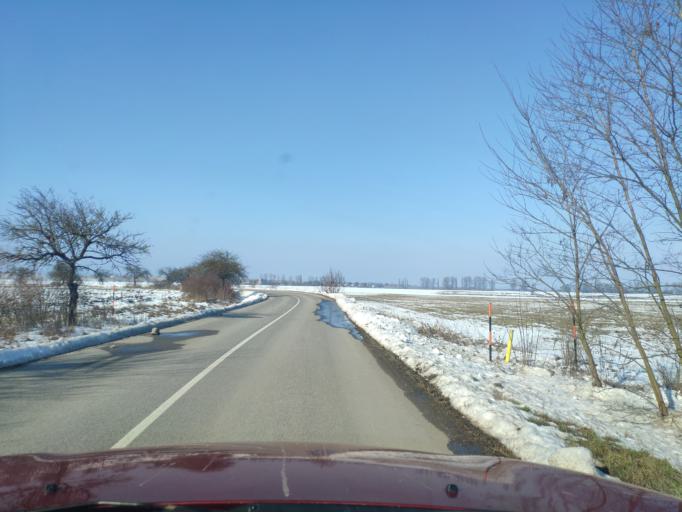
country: HU
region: Borsod-Abauj-Zemplen
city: Gonc
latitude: 48.5846
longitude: 21.2670
